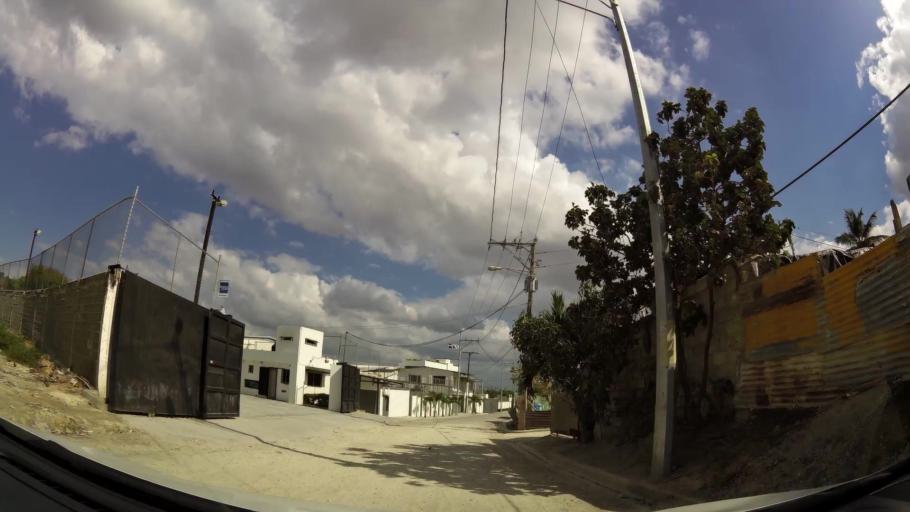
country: DO
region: Nacional
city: Ensanche Luperon
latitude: 18.5302
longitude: -69.8924
